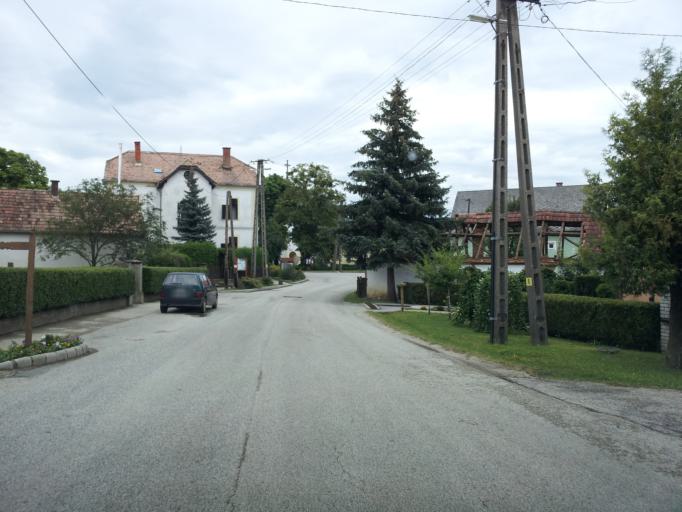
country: HU
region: Vas
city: Vasvar
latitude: 46.9810
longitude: 16.7416
